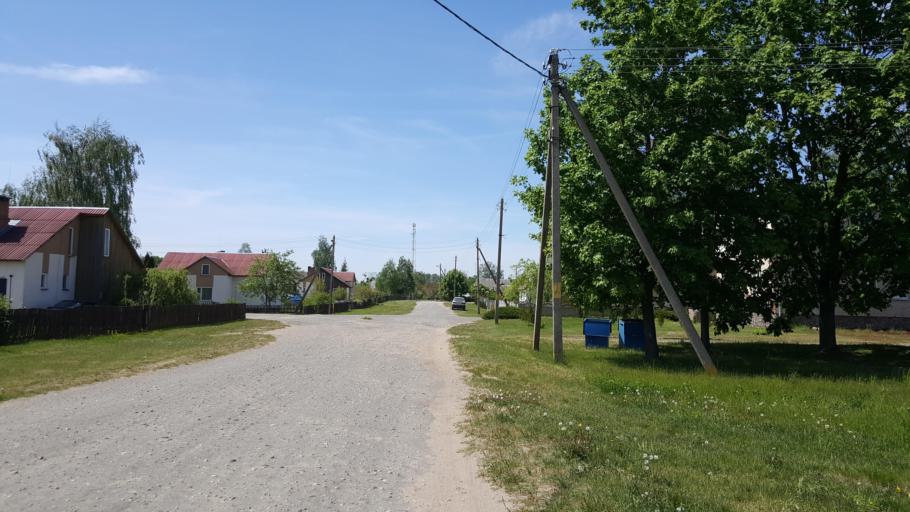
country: BY
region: Brest
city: Kobryn
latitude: 52.3391
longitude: 24.2510
